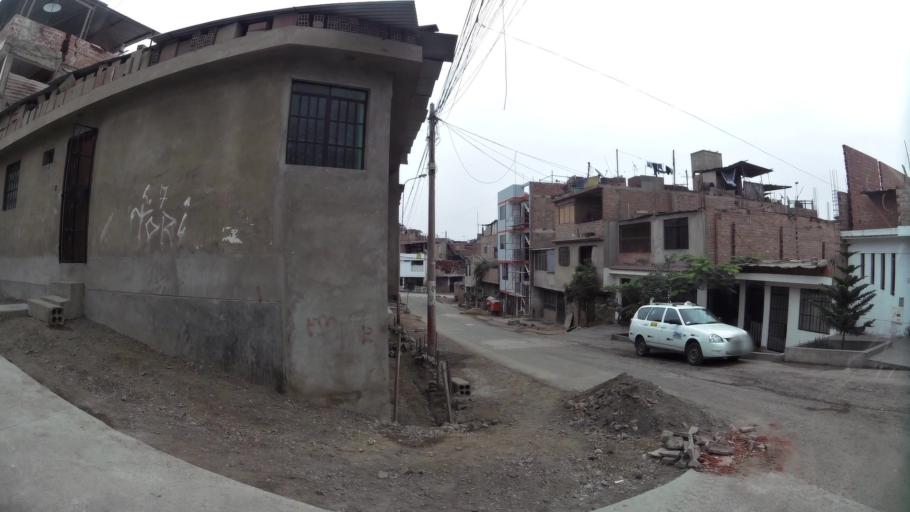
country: PE
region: Lima
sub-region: Lima
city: Surco
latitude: -12.1779
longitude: -76.9644
